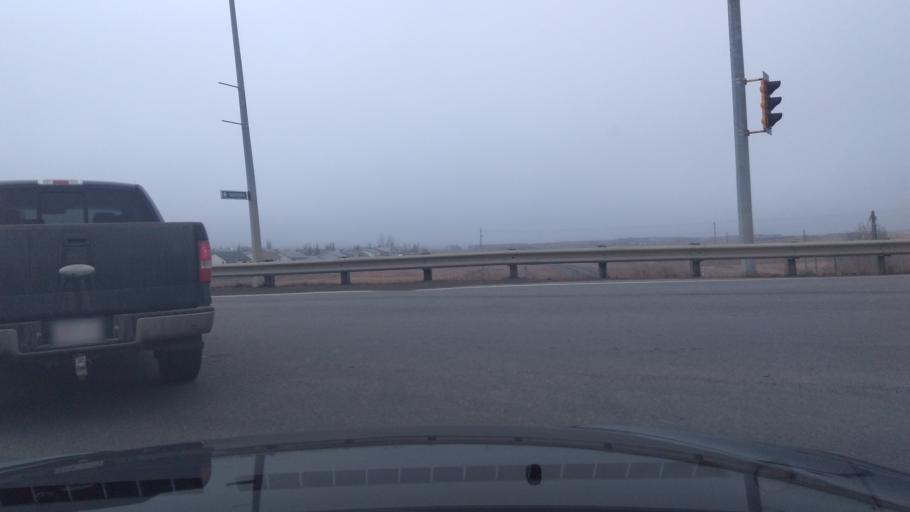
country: CA
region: Alberta
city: Cochrane
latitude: 51.1983
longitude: -114.4862
